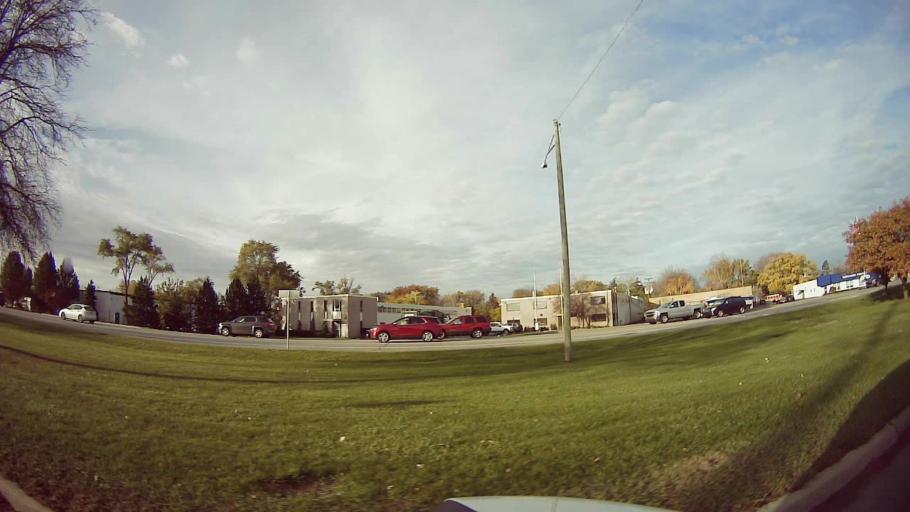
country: US
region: Michigan
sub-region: Oakland County
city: Clawson
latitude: 42.5543
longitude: -83.1260
